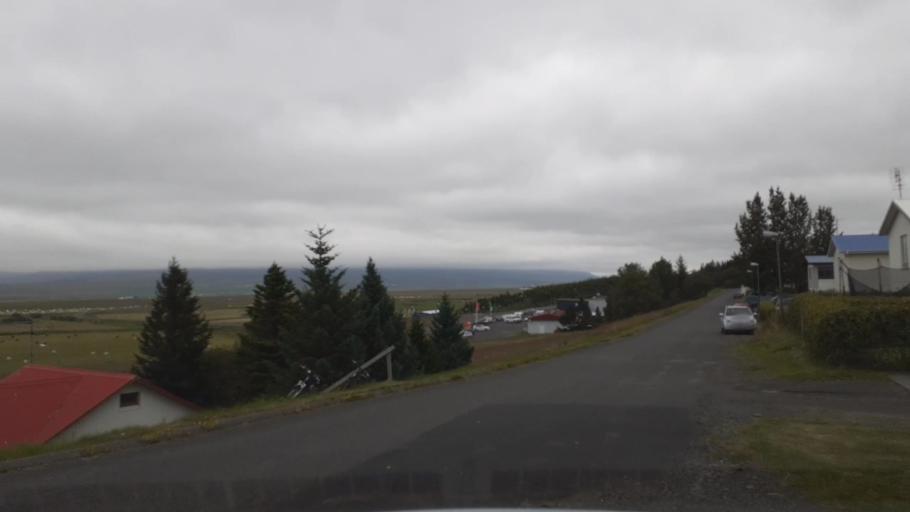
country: IS
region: Northwest
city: Saudarkrokur
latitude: 65.5551
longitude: -19.4507
